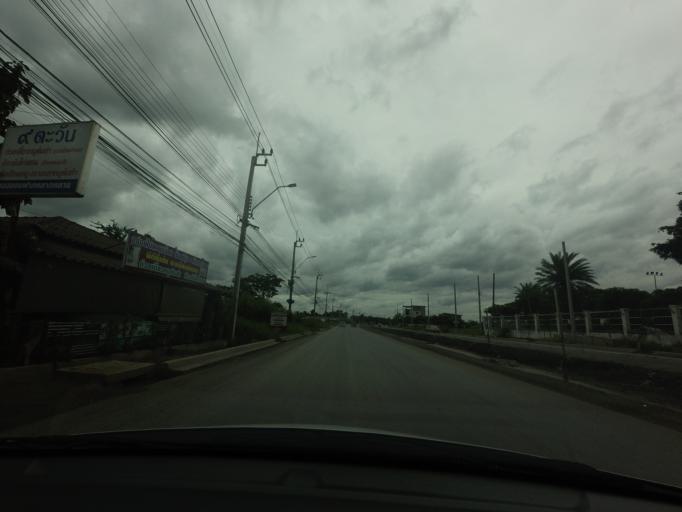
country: TH
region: Bangkok
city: Lat Krabang
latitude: 13.7734
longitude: 100.7765
